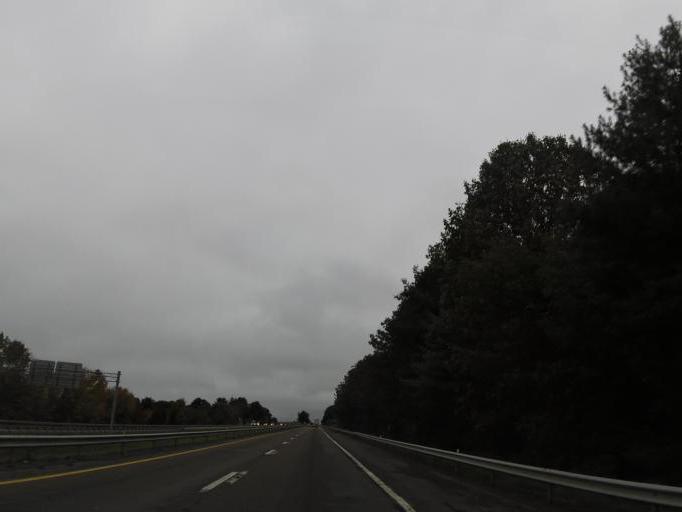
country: US
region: Virginia
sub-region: Wythe County
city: Wytheville
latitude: 36.9649
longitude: -81.0831
